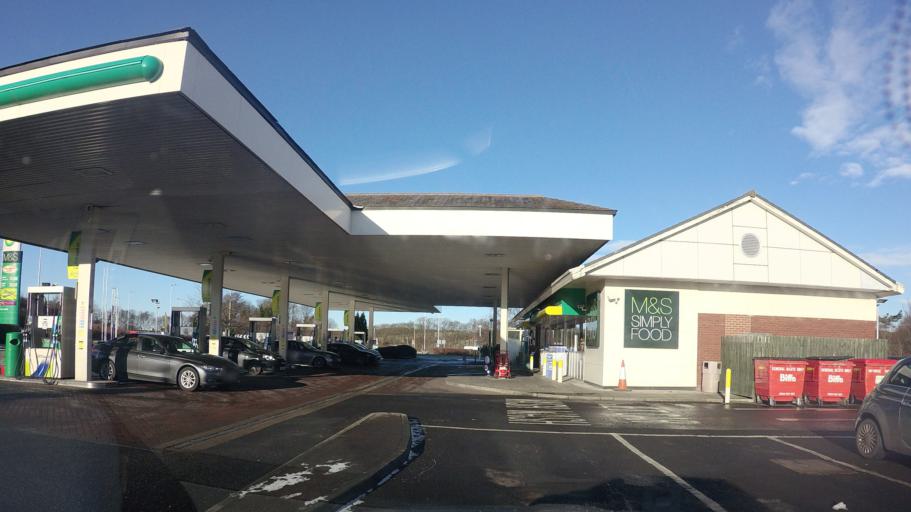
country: GB
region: Scotland
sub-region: Fife
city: Inverkeithing
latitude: 56.0409
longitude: -3.3665
